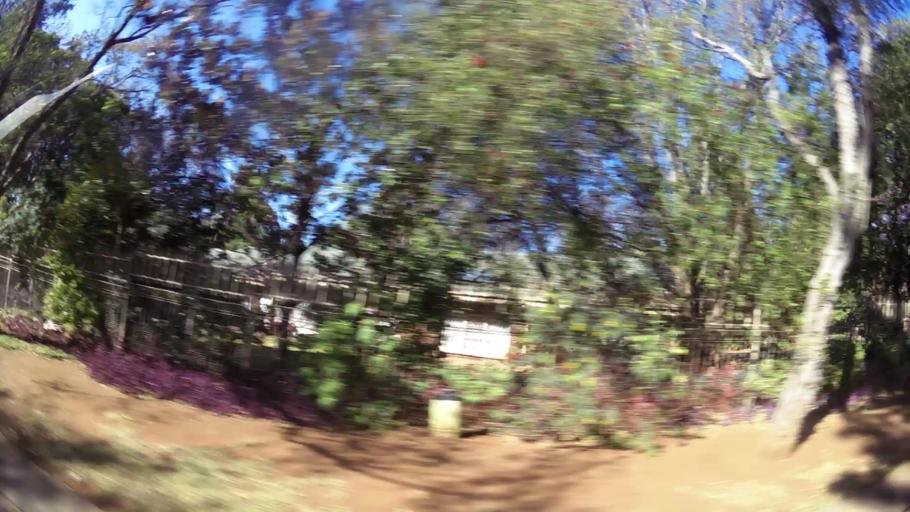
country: ZA
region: Gauteng
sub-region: City of Tshwane Metropolitan Municipality
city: Centurion
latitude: -25.8449
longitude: 28.2116
